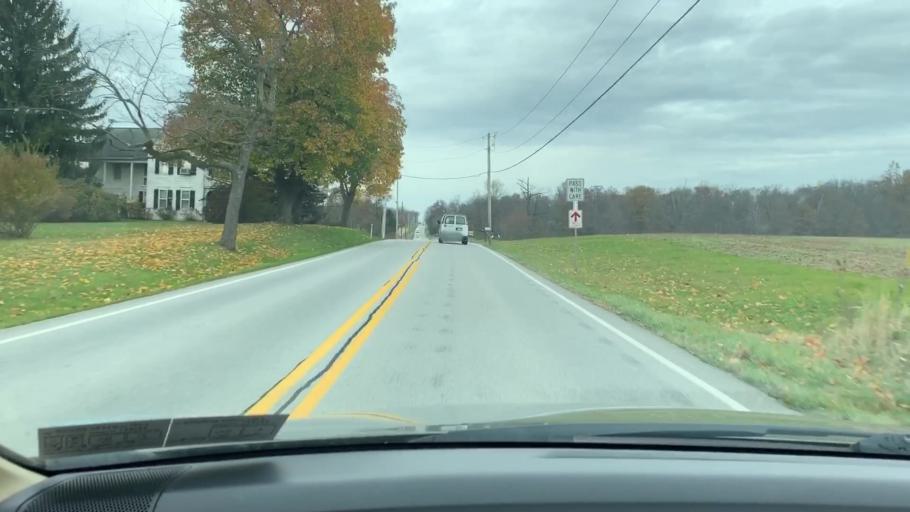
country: US
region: Pennsylvania
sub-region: Adams County
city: Lake Meade
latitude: 39.9446
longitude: -77.0844
